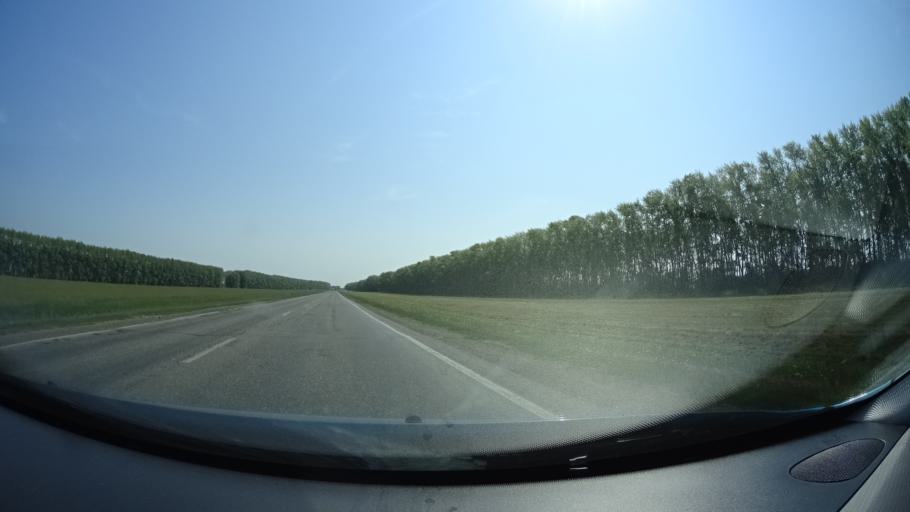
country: RU
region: Bashkortostan
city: Karmaskaly
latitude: 54.3962
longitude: 56.1063
